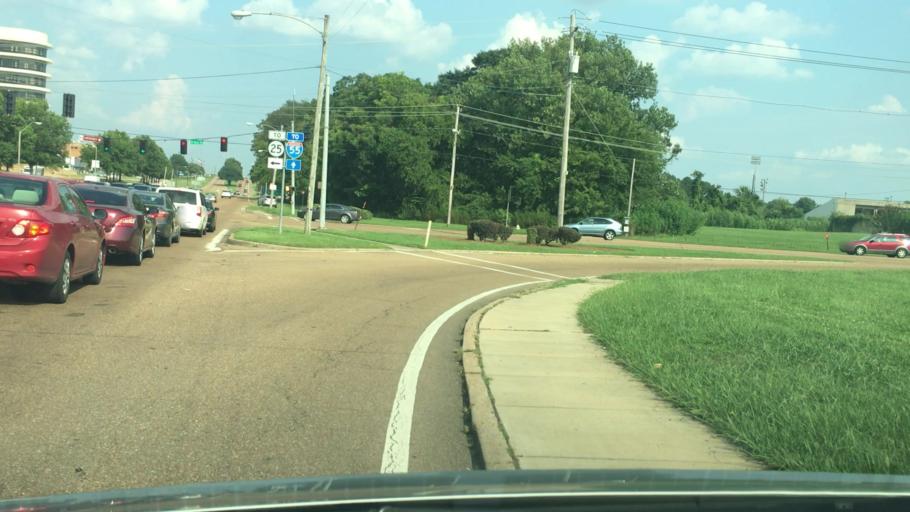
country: US
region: Mississippi
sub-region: Hinds County
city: Jackson
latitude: 32.3267
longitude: -90.1765
